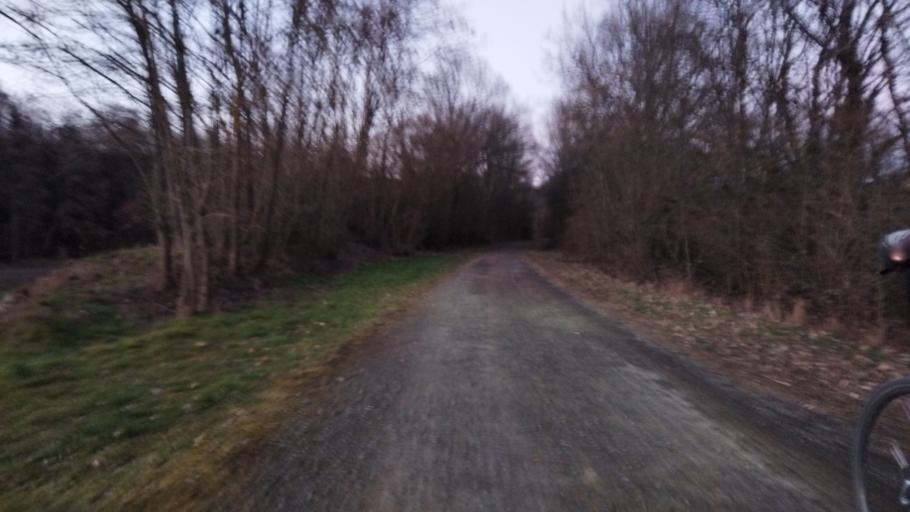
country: DE
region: Rheinland-Pfalz
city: Nanzdietschweiler
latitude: 49.4409
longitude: 7.4359
